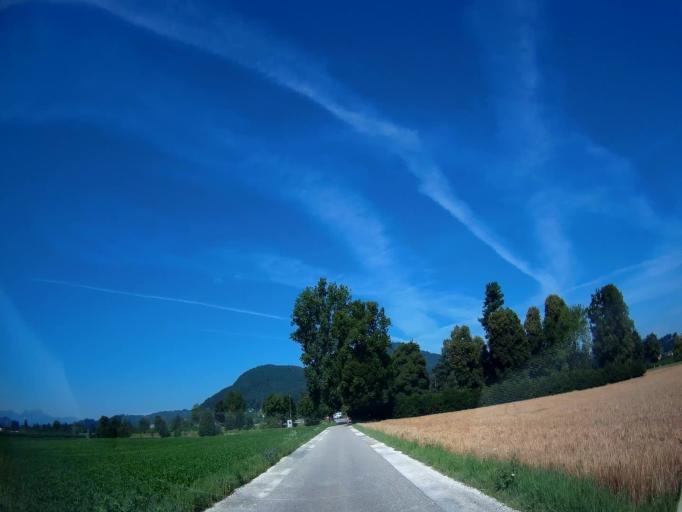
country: AT
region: Carinthia
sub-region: Politischer Bezirk Klagenfurt Land
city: Maria Saal
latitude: 46.6901
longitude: 14.3475
